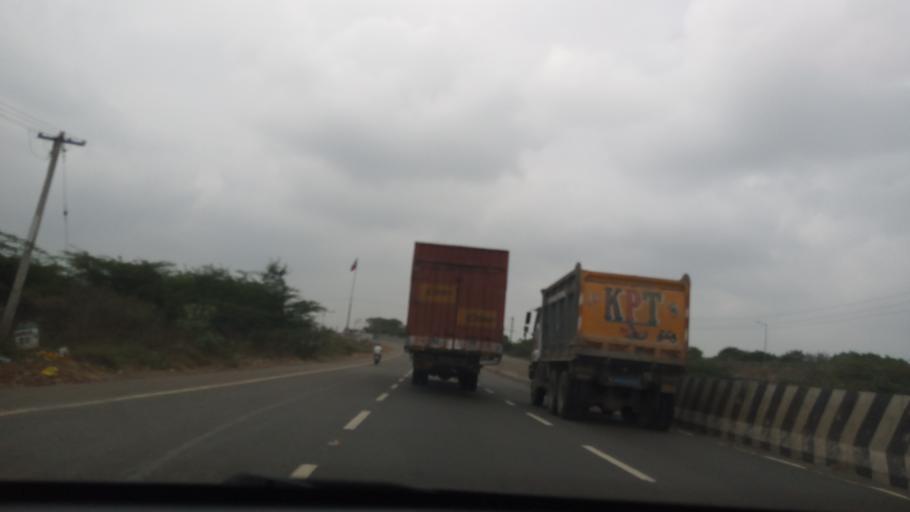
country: IN
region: Tamil Nadu
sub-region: Kancheepuram
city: Madambakkam
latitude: 12.8673
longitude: 79.9684
